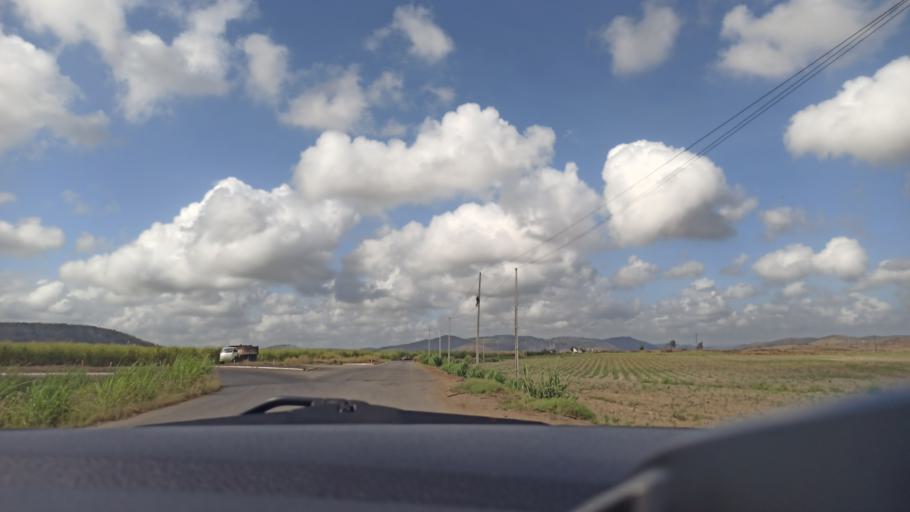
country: BR
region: Paraiba
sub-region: Juripiranga
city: Juripiranga
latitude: -7.3835
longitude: -35.2472
